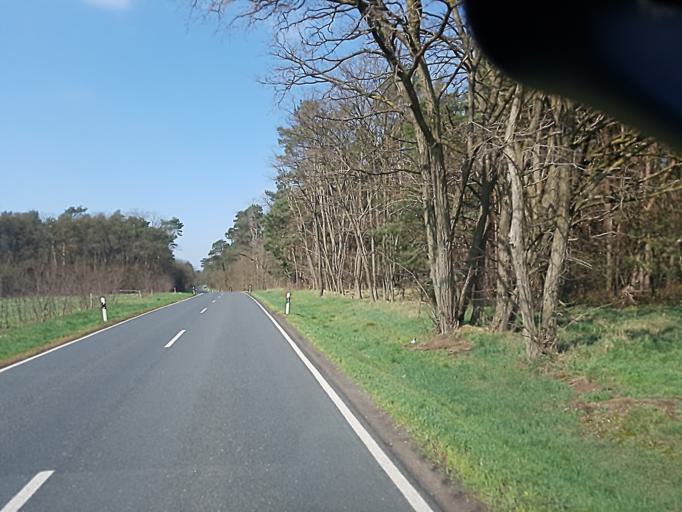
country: DE
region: Saxony
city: Kossa
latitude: 51.5787
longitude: 12.6832
